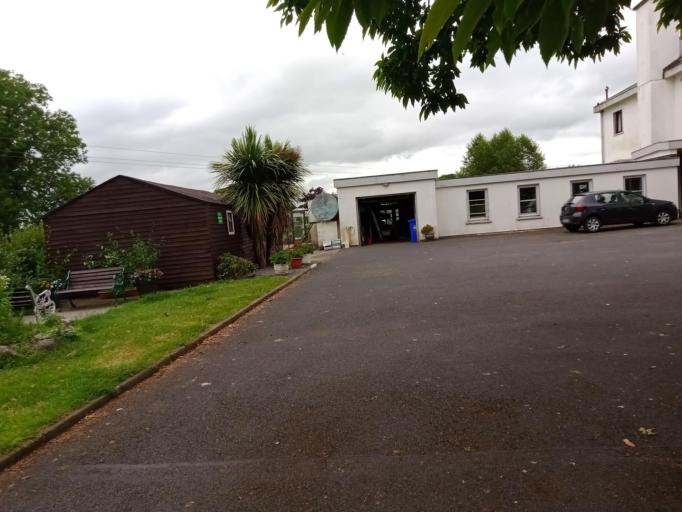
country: IE
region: Leinster
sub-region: Kilkenny
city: Callan
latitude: 52.5529
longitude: -7.3986
